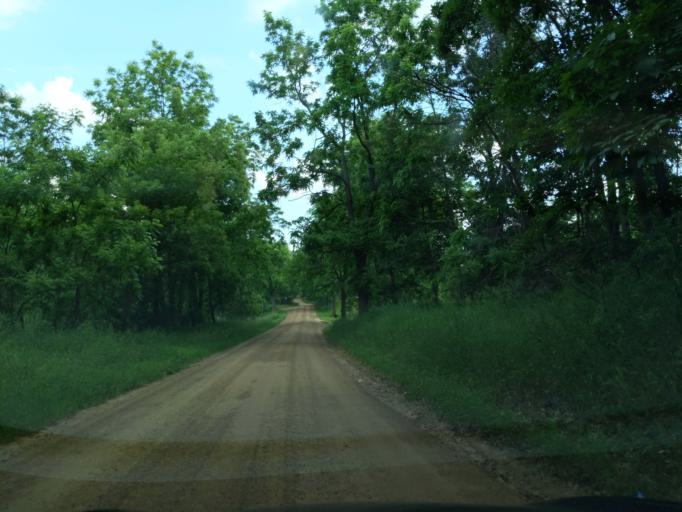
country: US
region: Michigan
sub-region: Shiawassee County
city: Laingsburg
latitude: 42.8367
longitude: -84.3692
